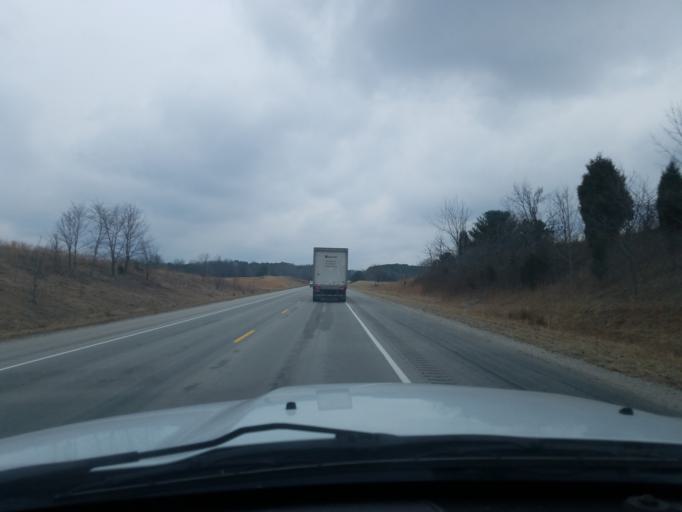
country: US
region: Indiana
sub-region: Perry County
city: Tell City
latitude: 38.0952
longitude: -86.6125
